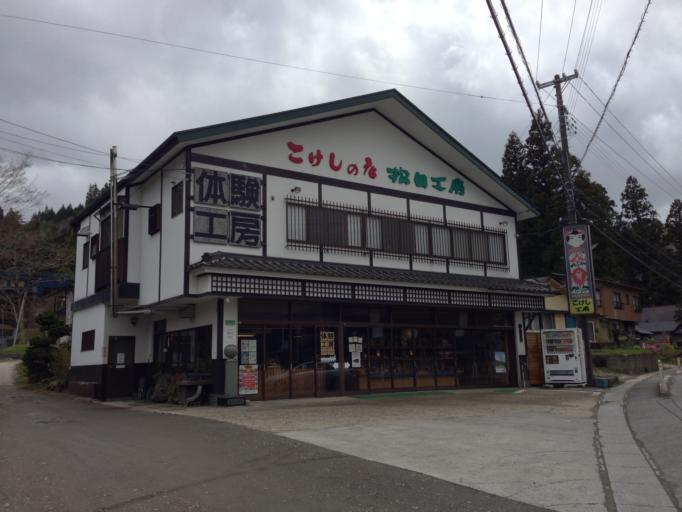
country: JP
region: Miyagi
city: Furukawa
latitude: 38.7377
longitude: 140.7083
